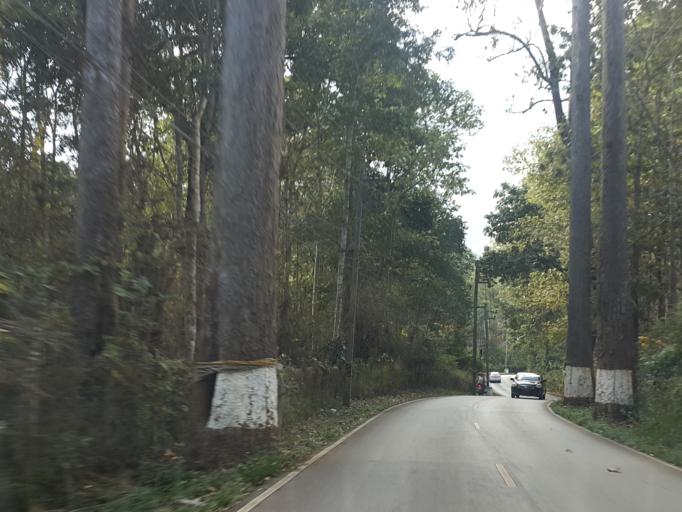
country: TH
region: Chiang Mai
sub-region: Amphoe Chiang Dao
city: Chiang Dao
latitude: 19.3839
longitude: 98.9391
